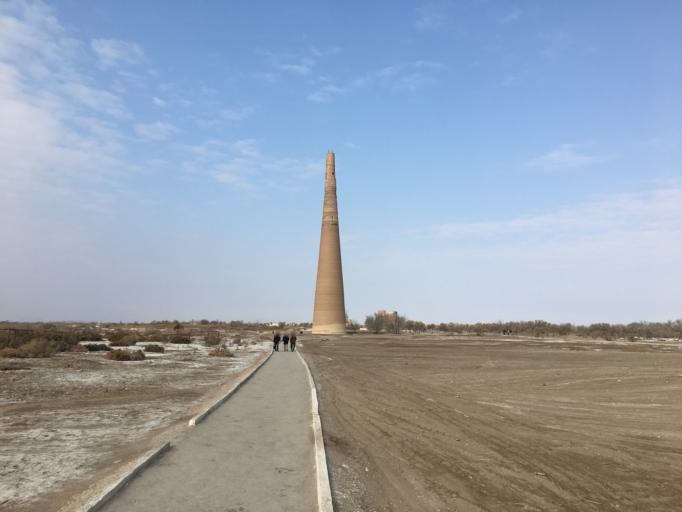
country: TM
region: Dasoguz
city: Koeneuergench
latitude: 42.3079
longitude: 59.1439
